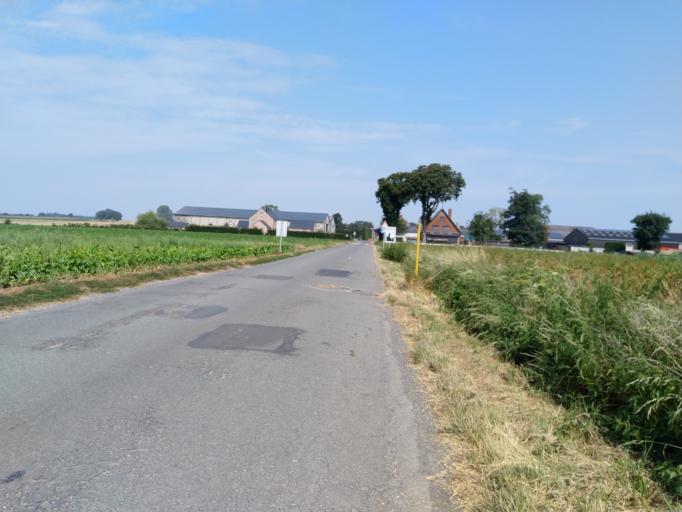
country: BE
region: Wallonia
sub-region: Province du Hainaut
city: Roeulx
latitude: 50.4863
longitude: 4.0576
